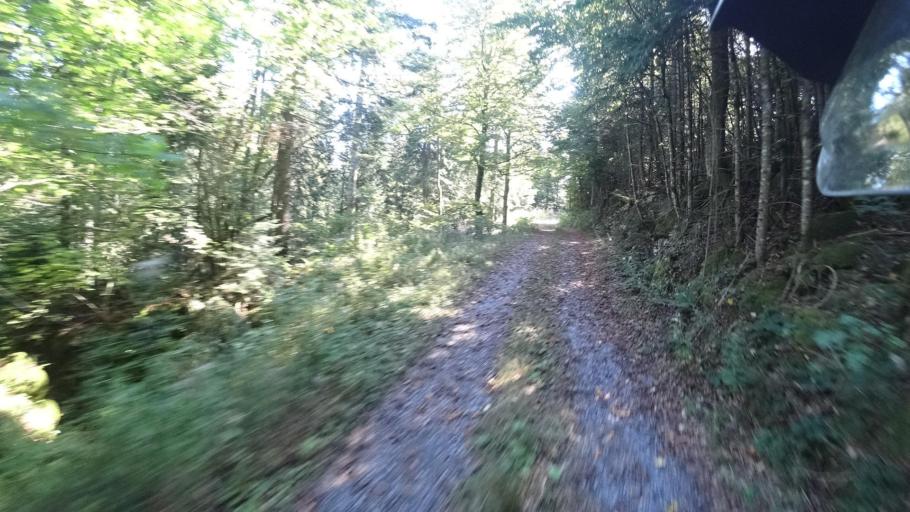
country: HR
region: Primorsko-Goranska
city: Vrbovsko
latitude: 45.2682
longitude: 15.1040
